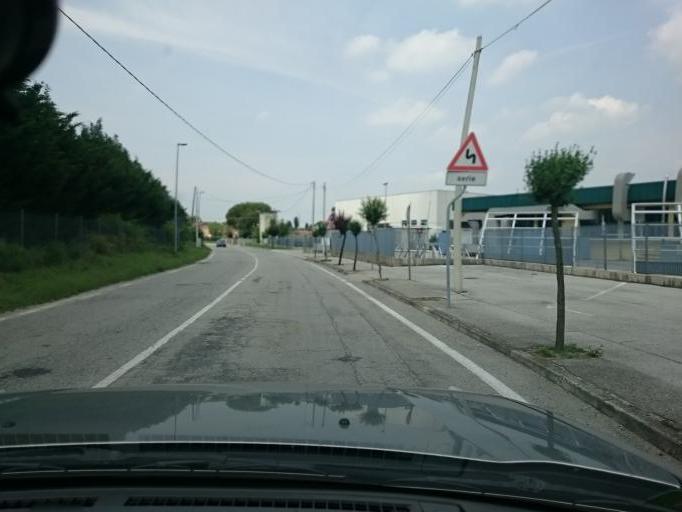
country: IT
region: Veneto
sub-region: Provincia di Padova
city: Sant'Angelo di Piove di Sacco
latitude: 45.3085
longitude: 11.9993
